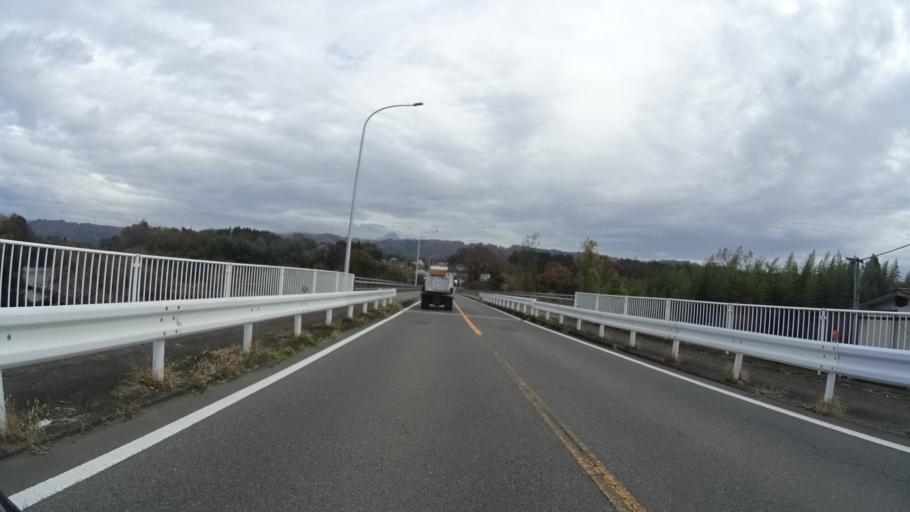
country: JP
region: Gunma
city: Shibukawa
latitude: 36.5459
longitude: 139.0294
